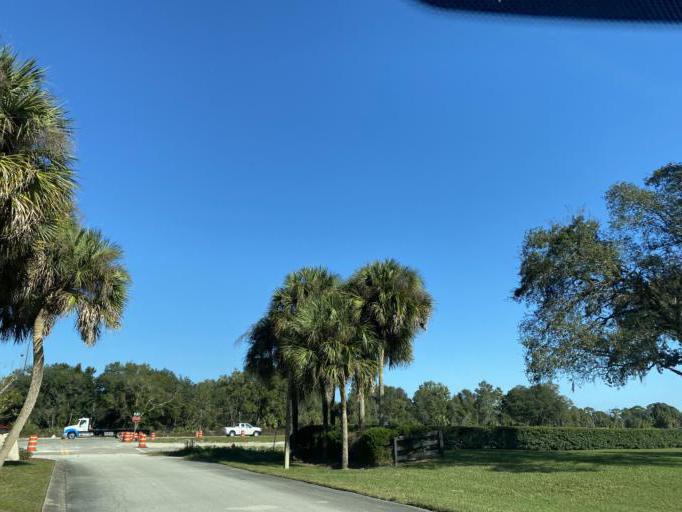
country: US
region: Florida
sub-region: Seminole County
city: Heathrow
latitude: 28.8142
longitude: -81.4002
